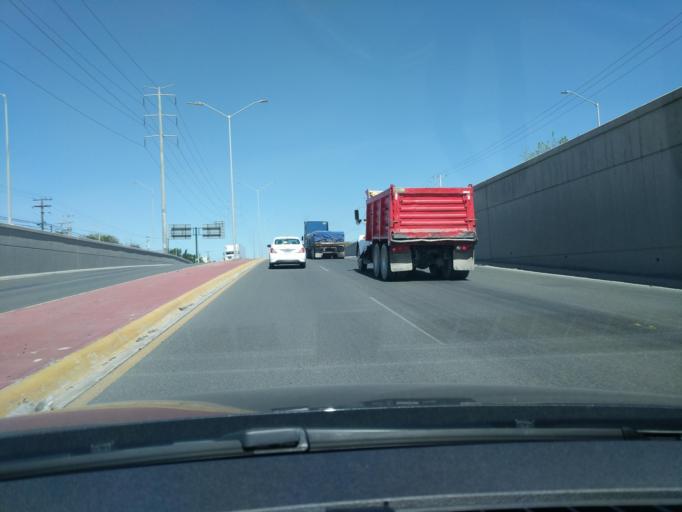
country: MX
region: Nuevo Leon
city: Apodaca
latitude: 25.7685
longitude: -100.1973
